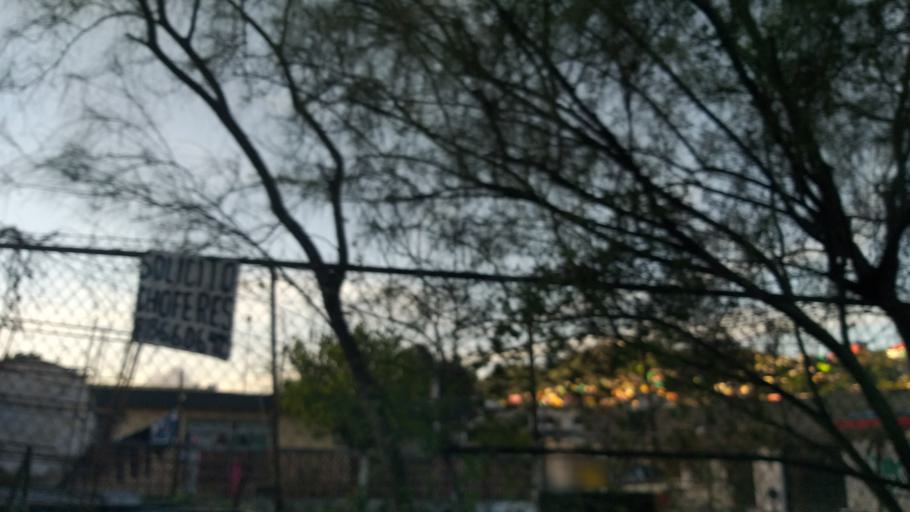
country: MX
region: Nuevo Leon
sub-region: Monterrey
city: Monterrey
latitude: 25.6378
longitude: -100.3093
